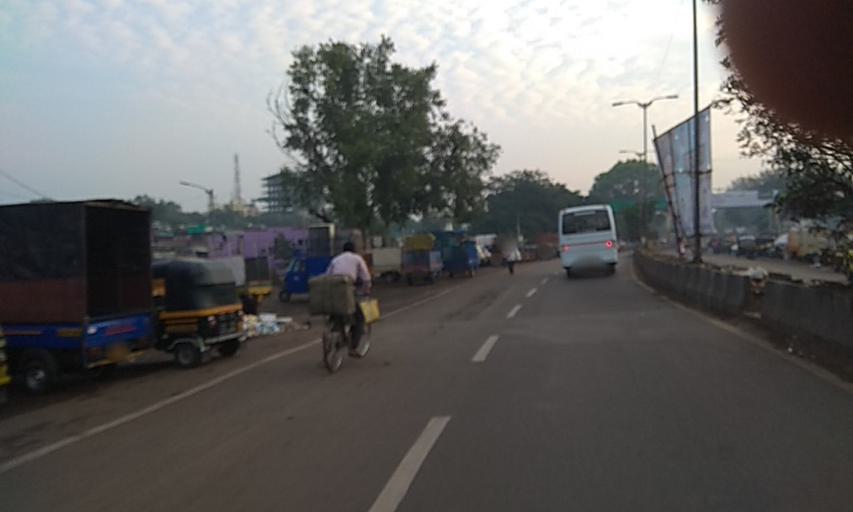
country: IN
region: Maharashtra
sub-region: Pune Division
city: Pune
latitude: 18.5266
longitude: 73.8614
